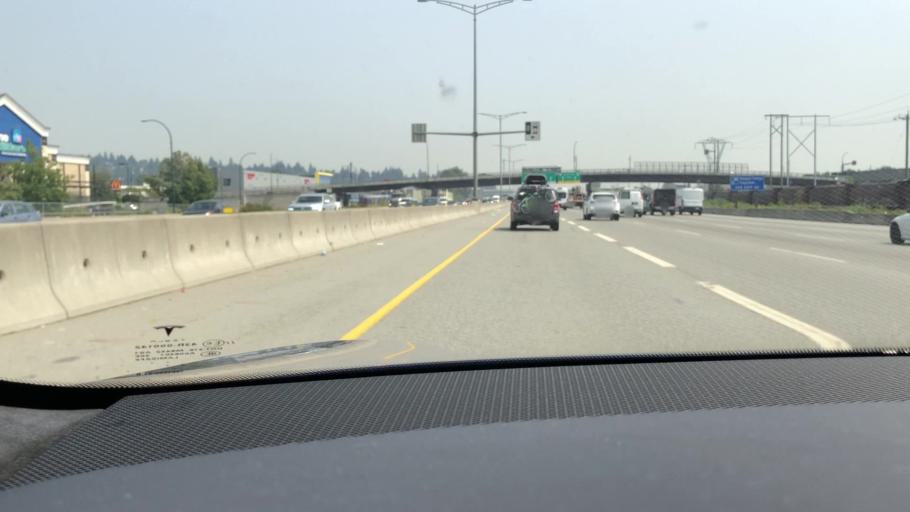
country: CA
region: British Columbia
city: Port Moody
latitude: 49.2327
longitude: -122.8653
